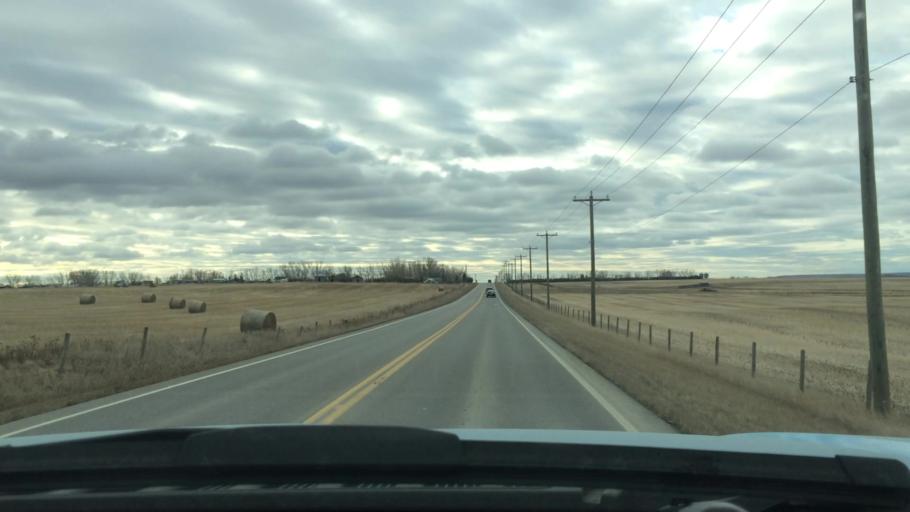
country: CA
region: Alberta
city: Airdrie
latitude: 51.2377
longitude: -114.0250
